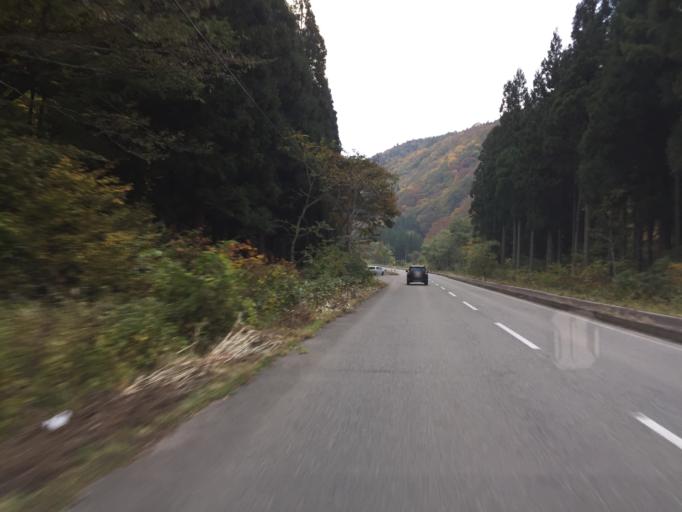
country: JP
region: Yamagata
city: Yonezawa
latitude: 37.8232
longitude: 140.0038
